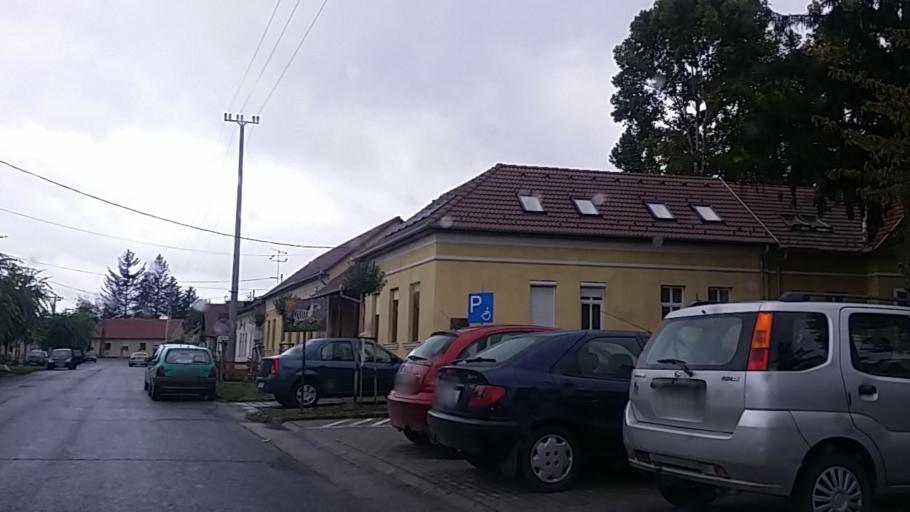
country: HU
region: Pest
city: Szob
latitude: 47.8180
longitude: 18.8665
